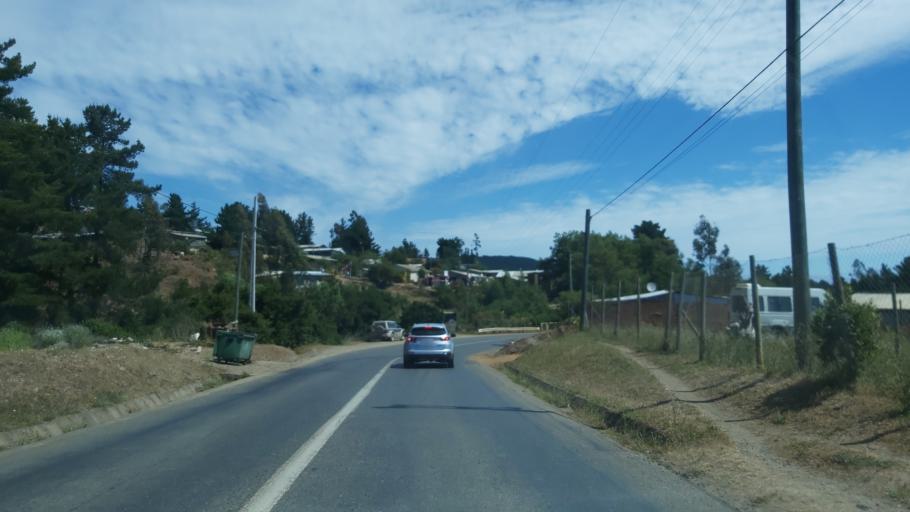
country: CL
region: Maule
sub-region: Provincia de Talca
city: Constitucion
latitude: -35.5029
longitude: -72.5187
